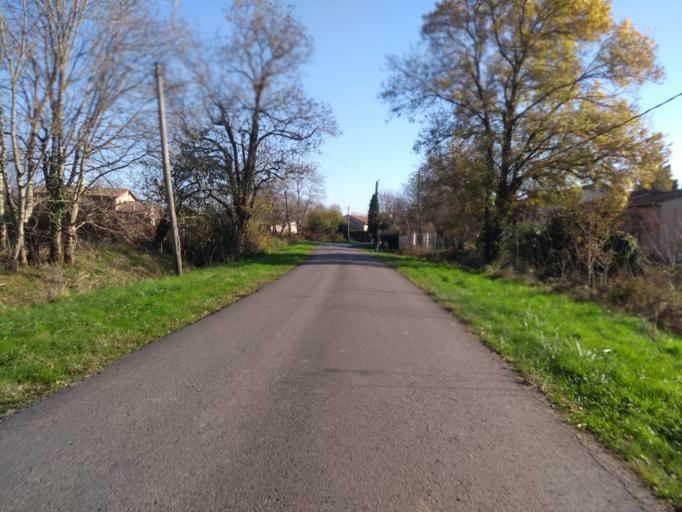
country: FR
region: Aquitaine
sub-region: Departement de la Gironde
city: Cambes
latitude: 44.7282
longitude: -0.4753
